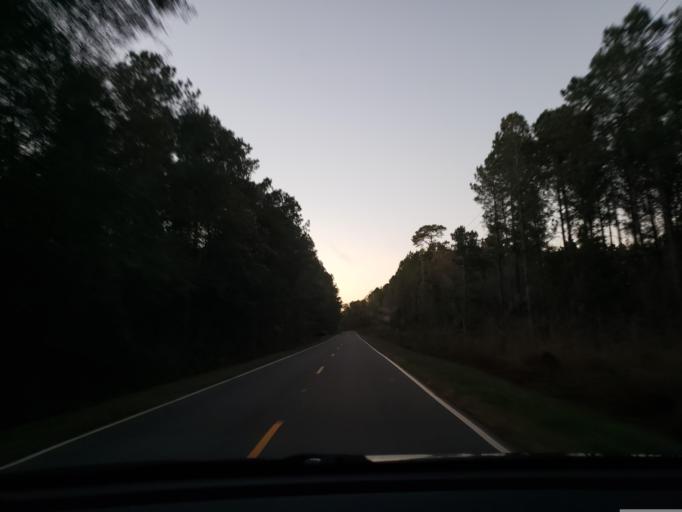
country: US
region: North Carolina
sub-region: Duplin County
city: Beulaville
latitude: 34.7849
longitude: -77.7559
